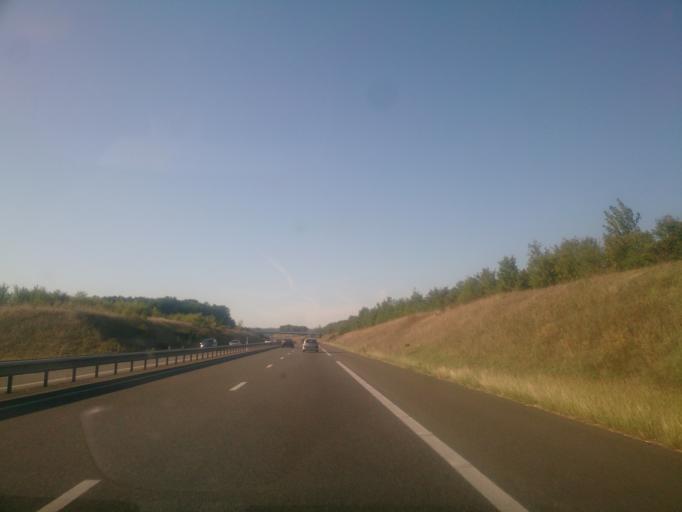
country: FR
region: Midi-Pyrenees
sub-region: Departement du Tarn-et-Garonne
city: Caussade
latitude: 44.2157
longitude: 1.5404
